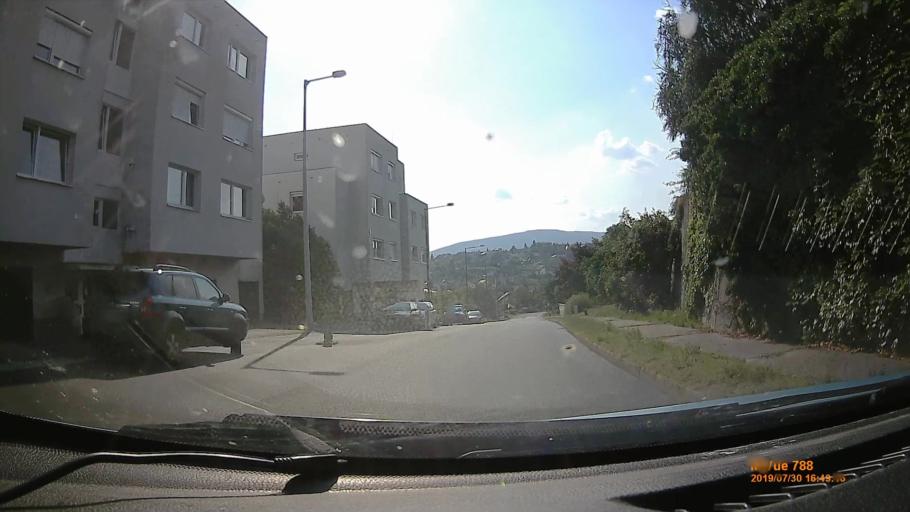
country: HU
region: Baranya
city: Pecs
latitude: 46.0837
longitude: 18.2129
